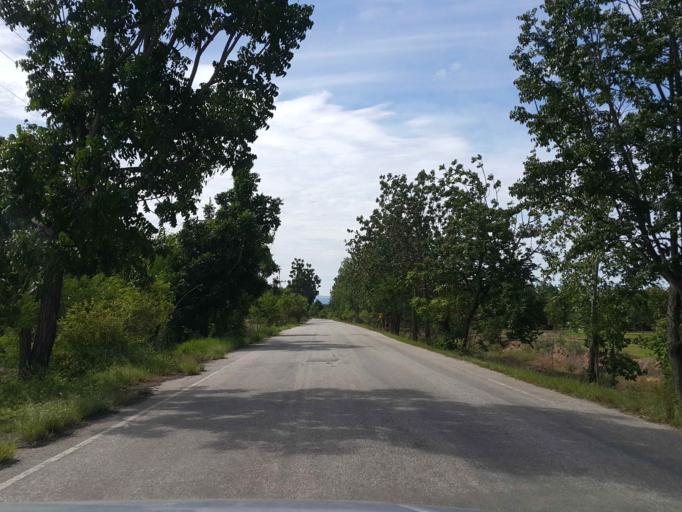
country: TH
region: Sukhothai
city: Ban Dan Lan Hoi
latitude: 17.1263
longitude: 99.5303
